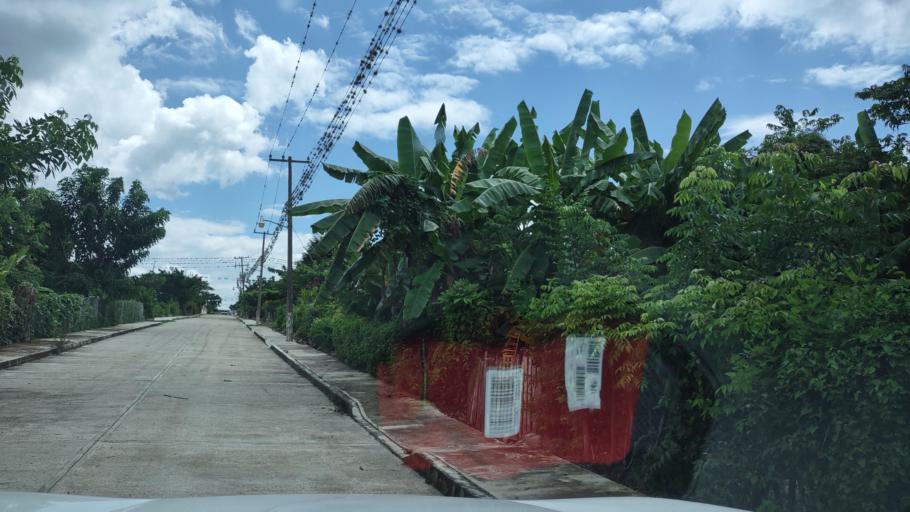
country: MX
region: Veracruz
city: Cerro Azul
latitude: 21.2436
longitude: -97.8010
